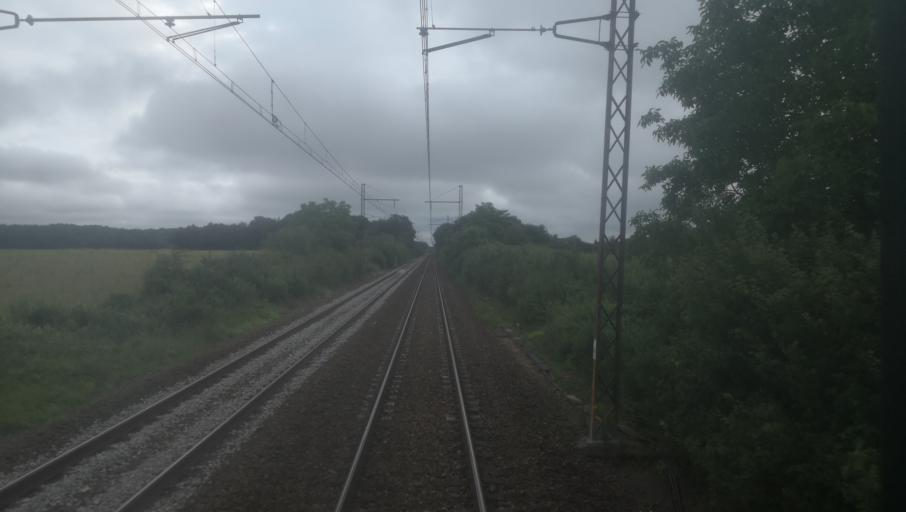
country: FR
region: Centre
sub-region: Departement de l'Indre
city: Deols
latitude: 46.8275
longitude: 1.7429
